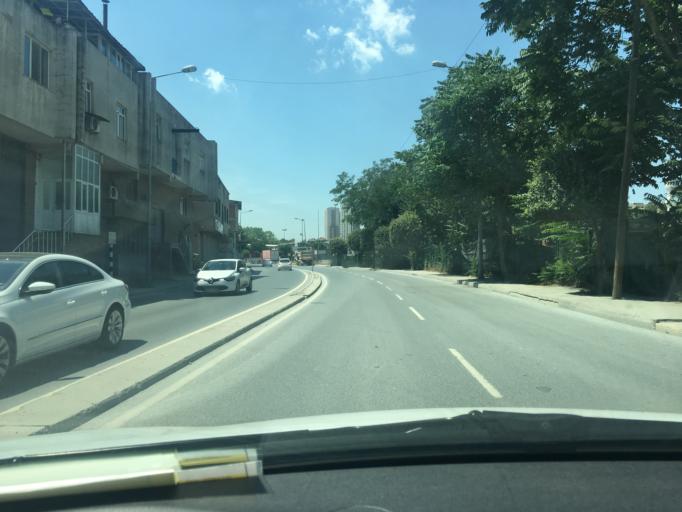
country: TR
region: Istanbul
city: Sisli
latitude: 41.0854
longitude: 28.9467
